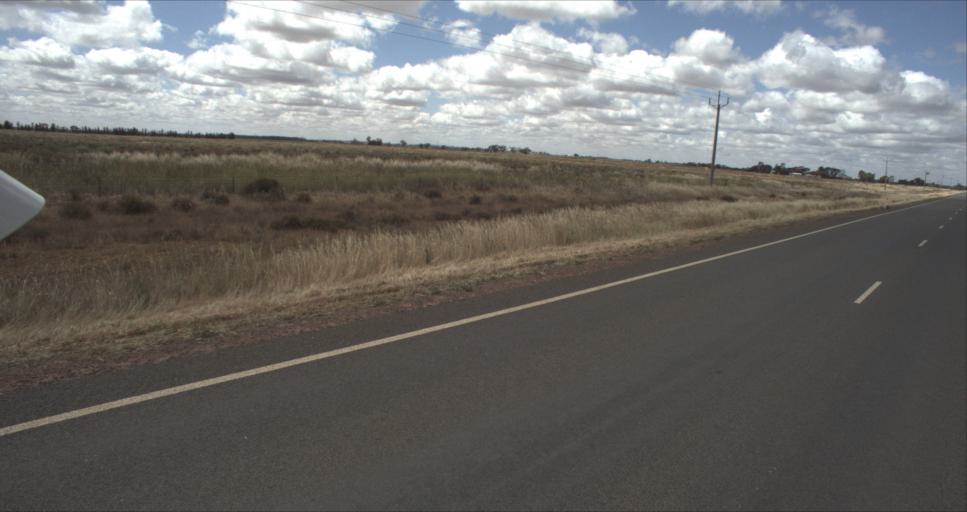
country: AU
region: New South Wales
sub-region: Murrumbidgee Shire
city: Darlington Point
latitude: -34.4885
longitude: 146.1623
